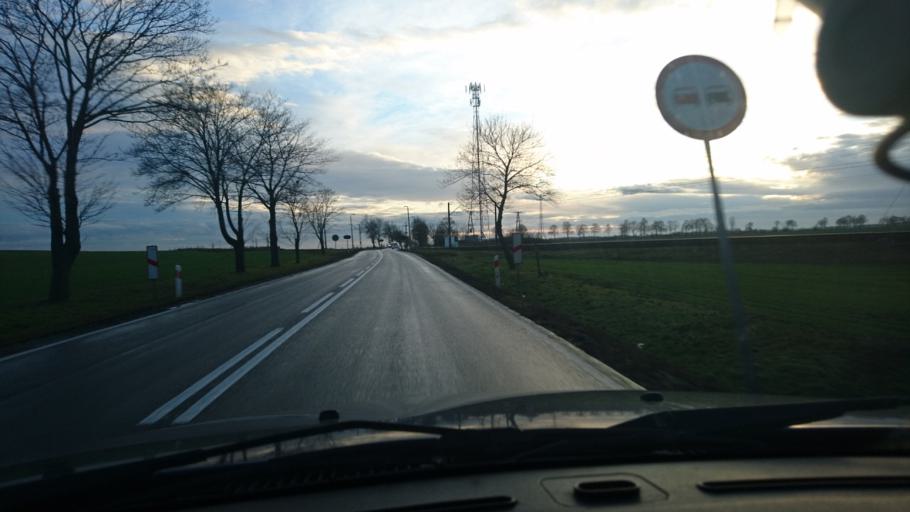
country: PL
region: Opole Voivodeship
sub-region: Powiat kluczborski
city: Byczyna
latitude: 51.0994
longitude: 18.2045
